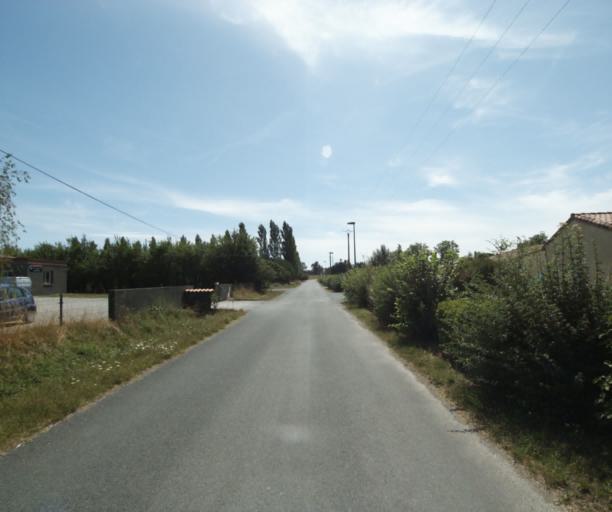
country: FR
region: Midi-Pyrenees
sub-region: Departement du Tarn
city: Puylaurens
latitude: 43.5174
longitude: 2.0121
